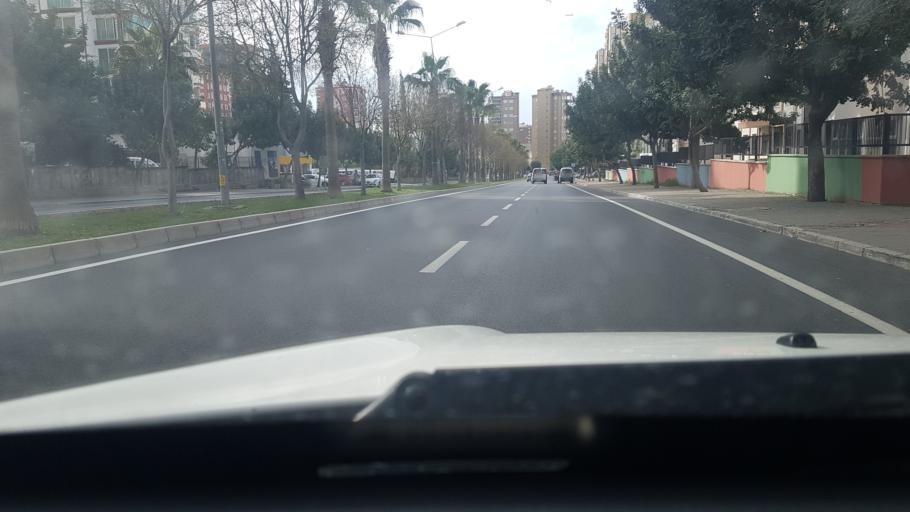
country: TR
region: Adana
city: Seyhan
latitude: 37.0345
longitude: 35.2810
